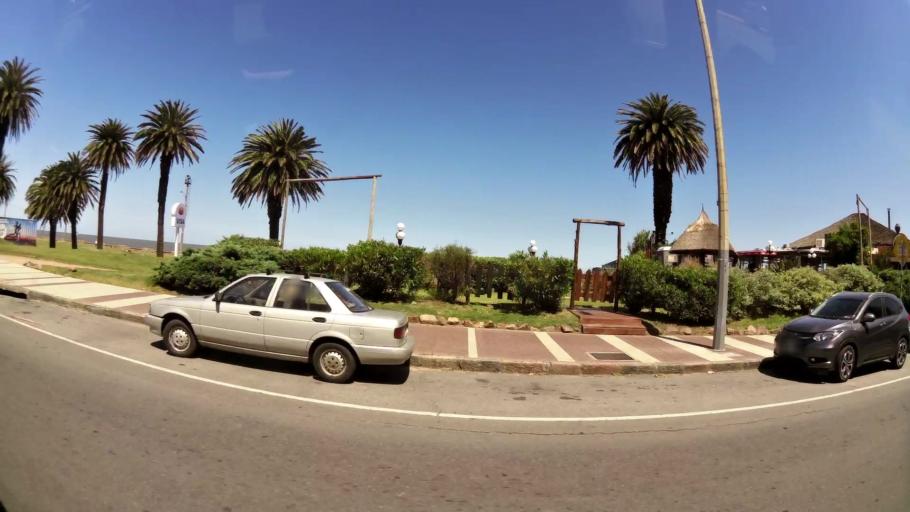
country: UY
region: Montevideo
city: Montevideo
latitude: -34.9209
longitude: -56.1495
